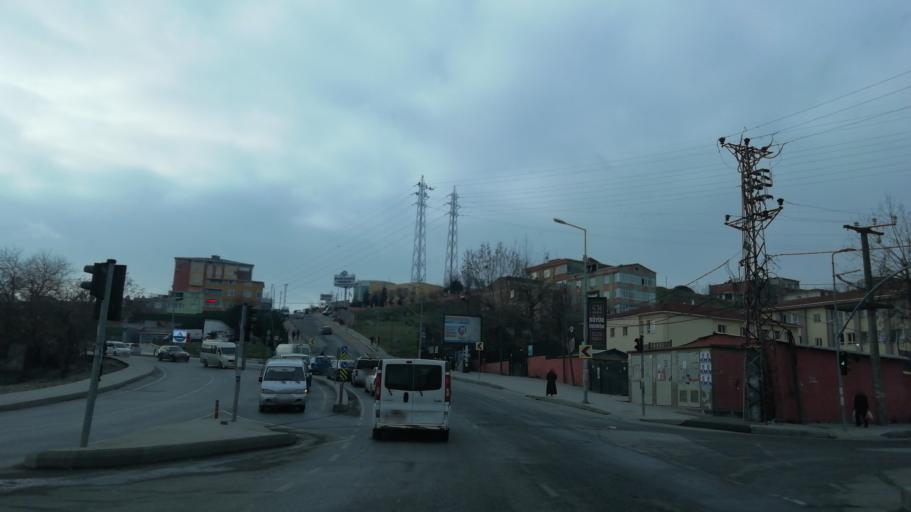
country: TR
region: Istanbul
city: Esenyurt
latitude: 41.0578
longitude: 28.7292
